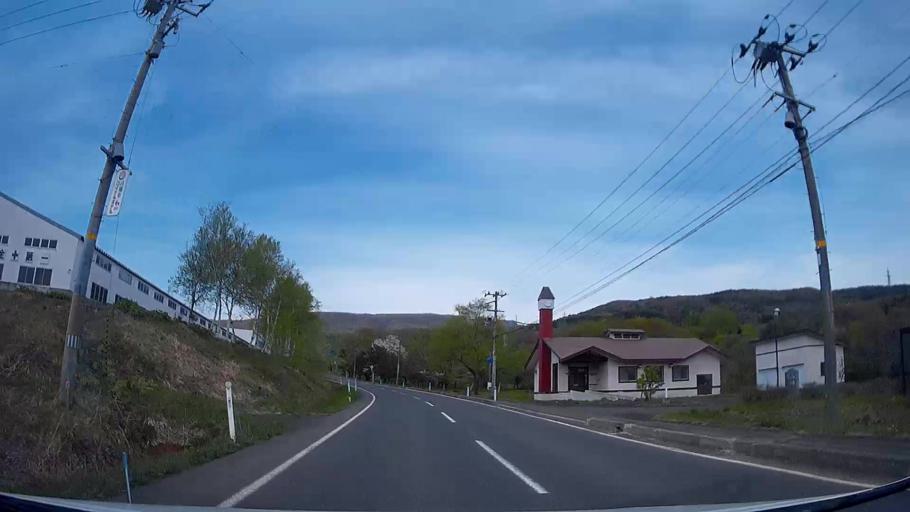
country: JP
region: Iwate
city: Shizukuishi
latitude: 39.9214
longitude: 140.9798
